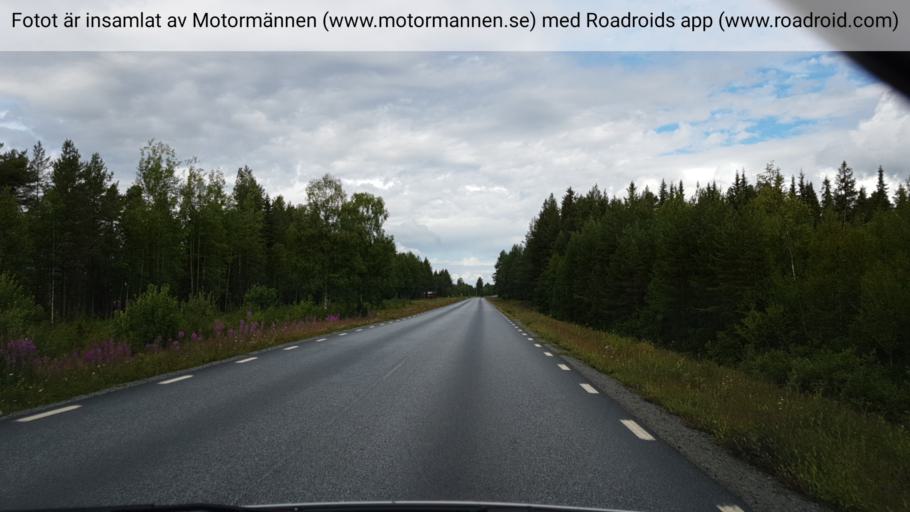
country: SE
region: Vaesterbotten
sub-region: Vilhelmina Kommun
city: Vilhelmina
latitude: 64.4725
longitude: 16.7952
